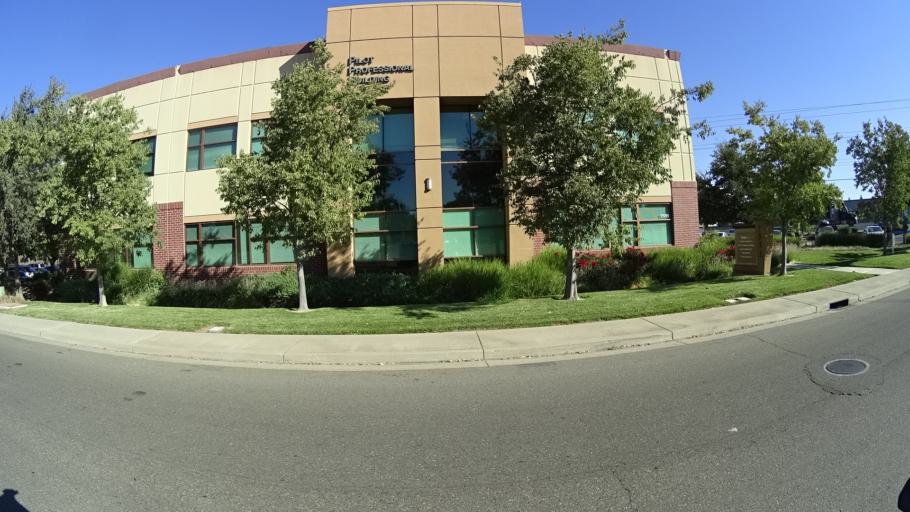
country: US
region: California
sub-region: Sacramento County
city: Florin
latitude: 38.4660
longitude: -121.4160
